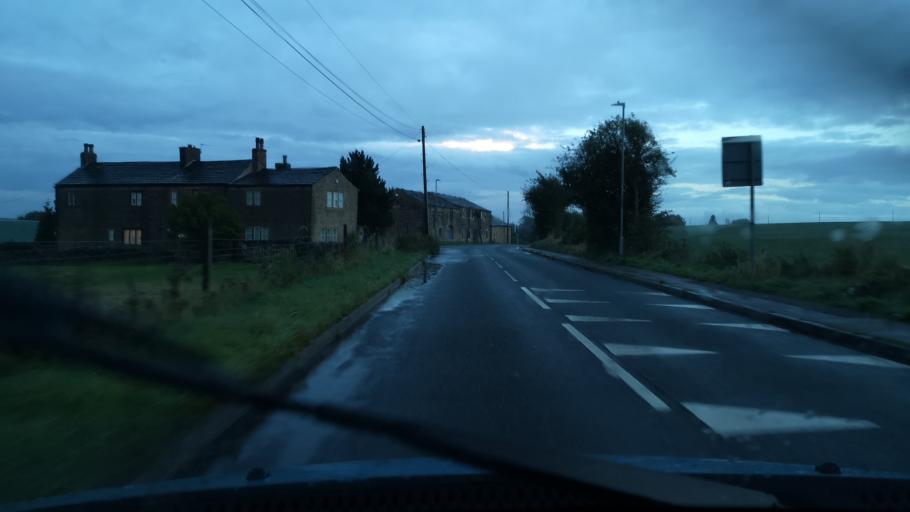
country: GB
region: England
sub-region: Kirklees
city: Batley
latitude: 53.7311
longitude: -1.6401
